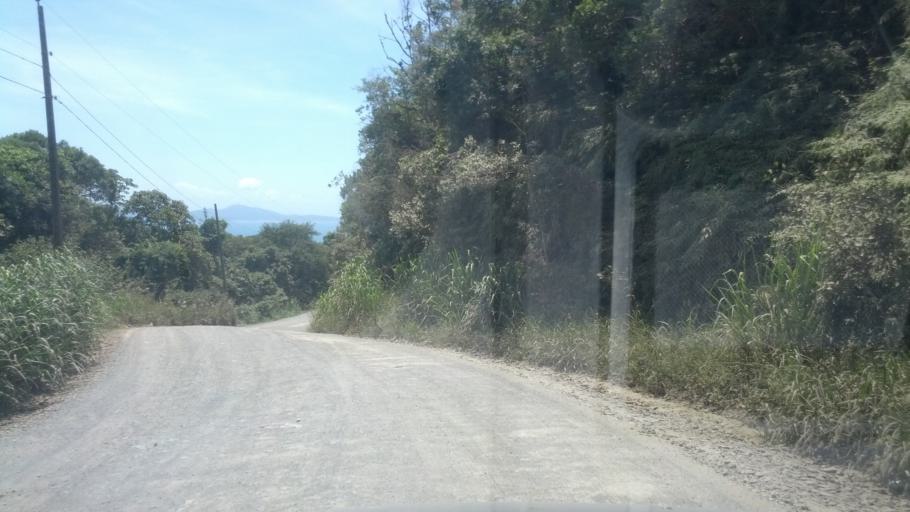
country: BR
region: Santa Catarina
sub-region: Porto Belo
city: Porto Belo
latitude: -27.1612
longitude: -48.5304
